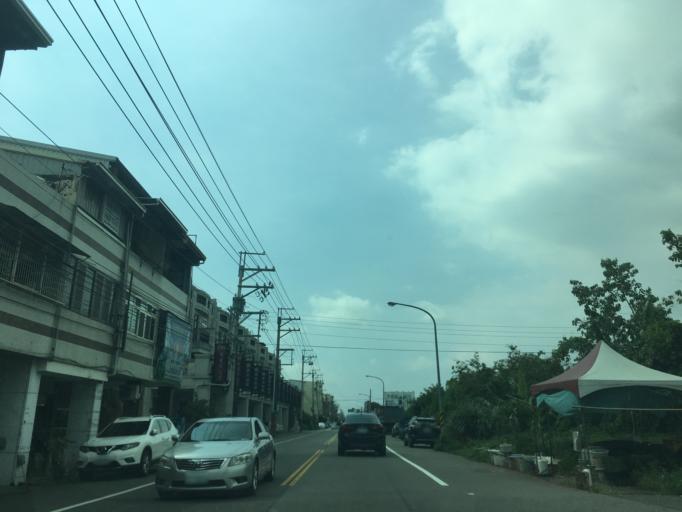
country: TW
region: Taiwan
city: Fengyuan
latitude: 24.2457
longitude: 120.8105
